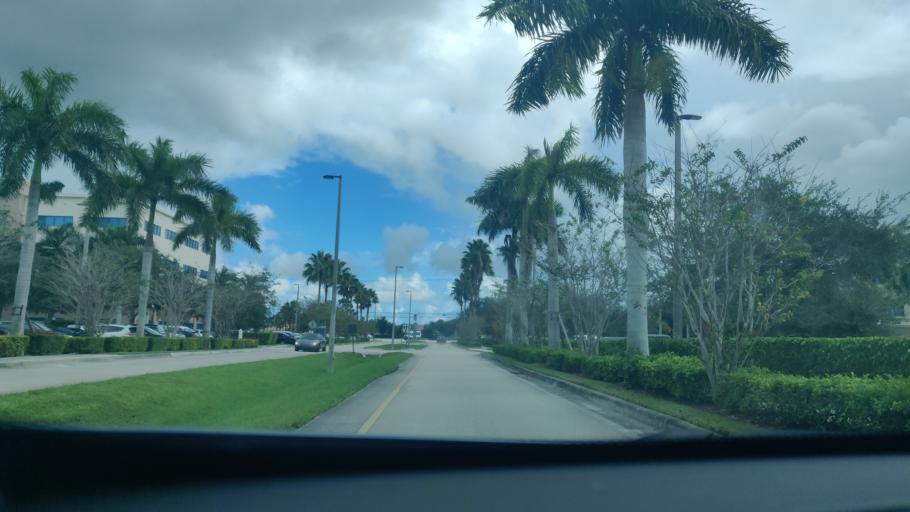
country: US
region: Florida
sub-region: Palm Beach County
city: Wellington
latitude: 26.6553
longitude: -80.2053
